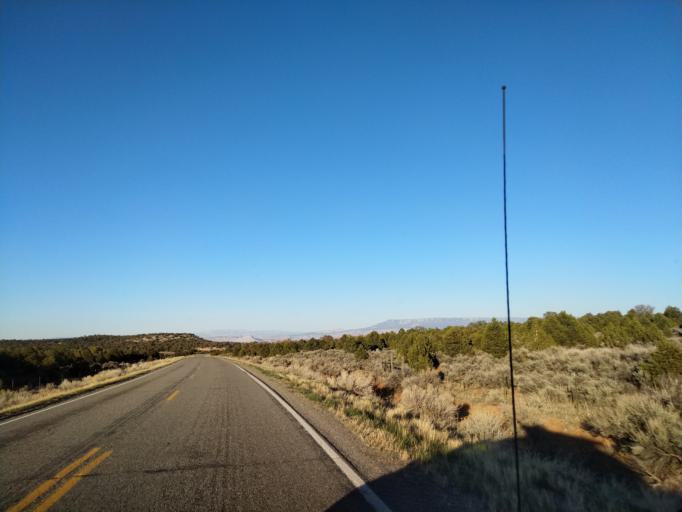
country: US
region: Colorado
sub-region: Mesa County
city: Redlands
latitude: 39.0058
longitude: -108.6886
